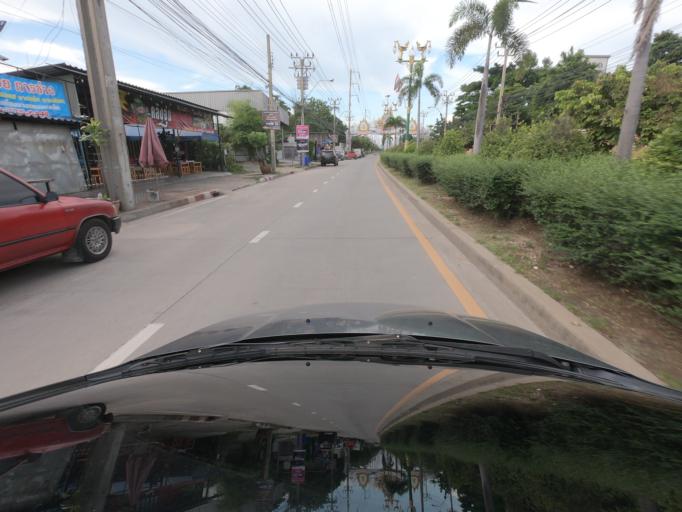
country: TH
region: Bangkok
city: Bang Na
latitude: 13.6536
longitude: 100.6206
